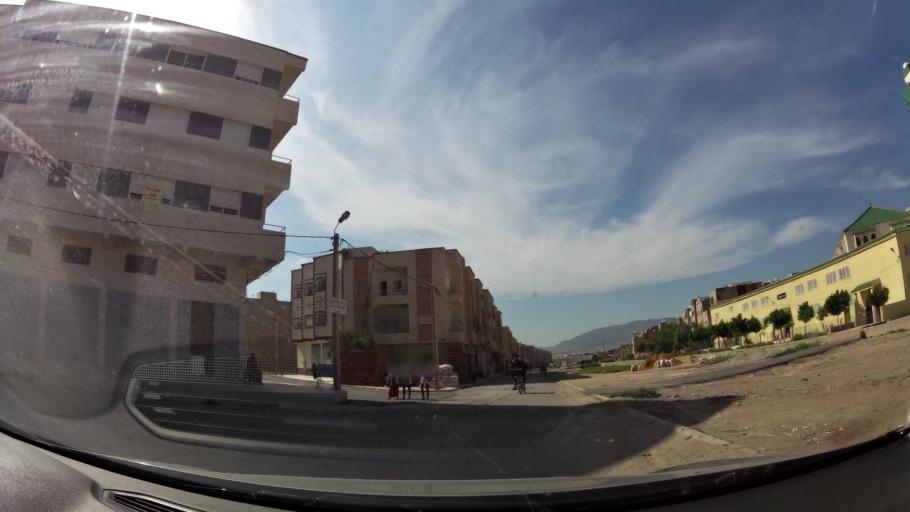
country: MA
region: Fes-Boulemane
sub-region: Fes
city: Fes
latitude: 34.0121
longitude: -5.0345
